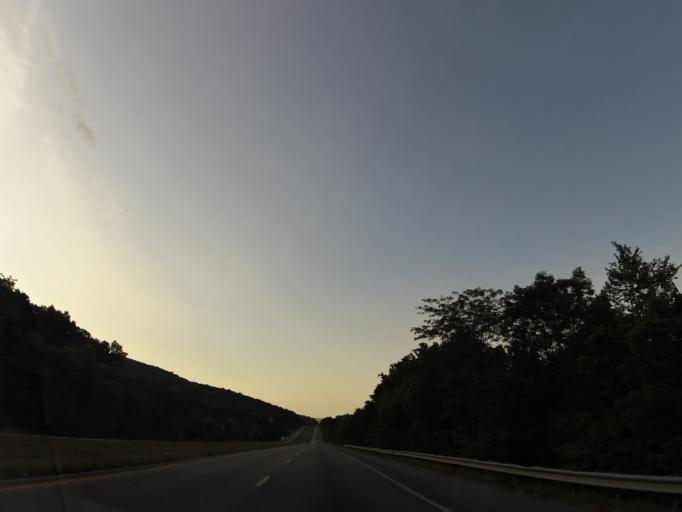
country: US
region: Georgia
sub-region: Dade County
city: Trenton
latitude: 34.7445
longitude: -85.5378
